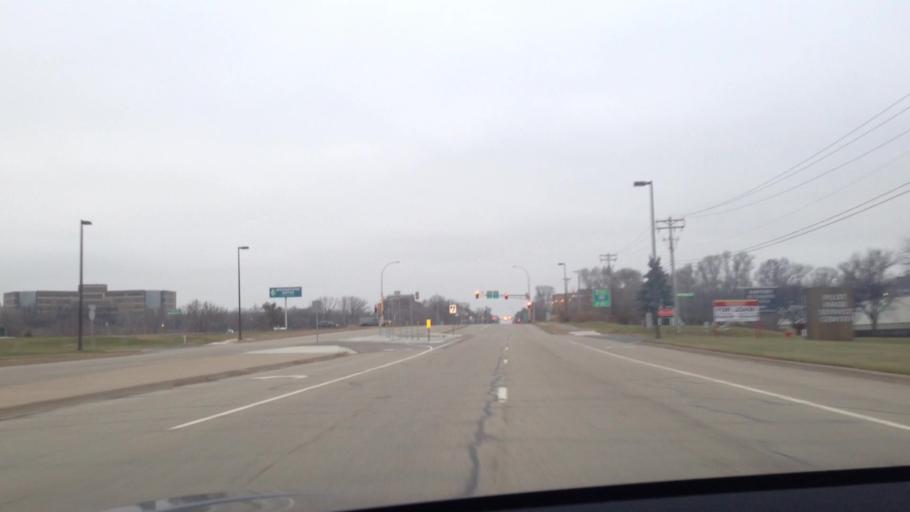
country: US
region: Minnesota
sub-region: Dakota County
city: Mendota Heights
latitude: 44.8643
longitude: -93.1673
